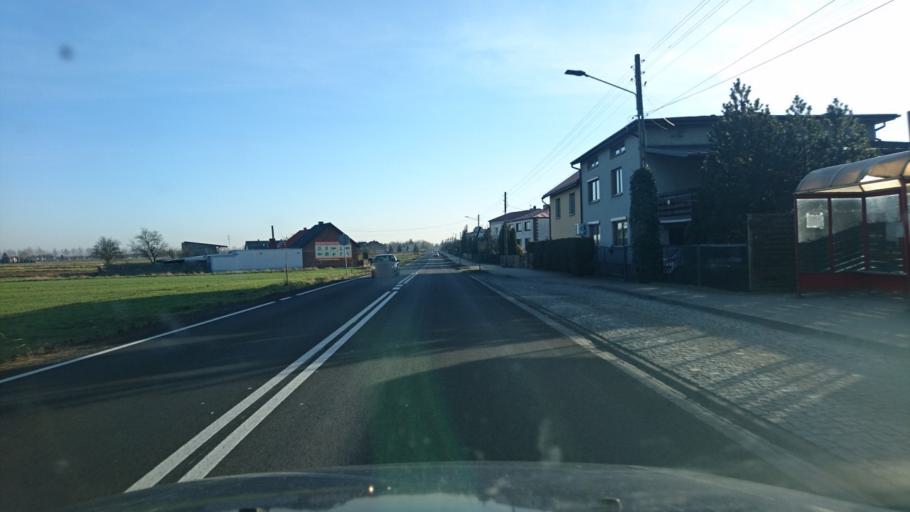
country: PL
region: Silesian Voivodeship
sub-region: Powiat klobucki
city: Starokrzepice
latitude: 51.0011
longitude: 18.6652
